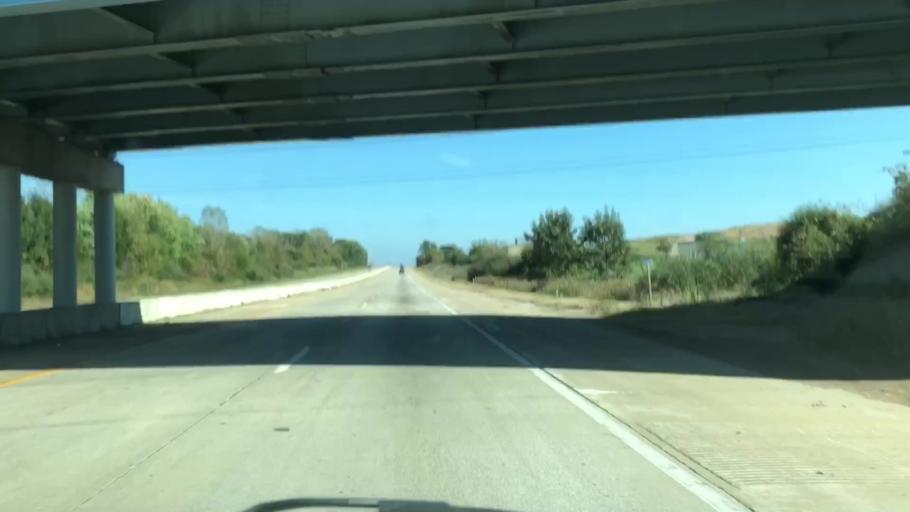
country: US
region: Indiana
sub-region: Elkhart County
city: Elkhart
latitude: 41.6356
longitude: -85.9845
